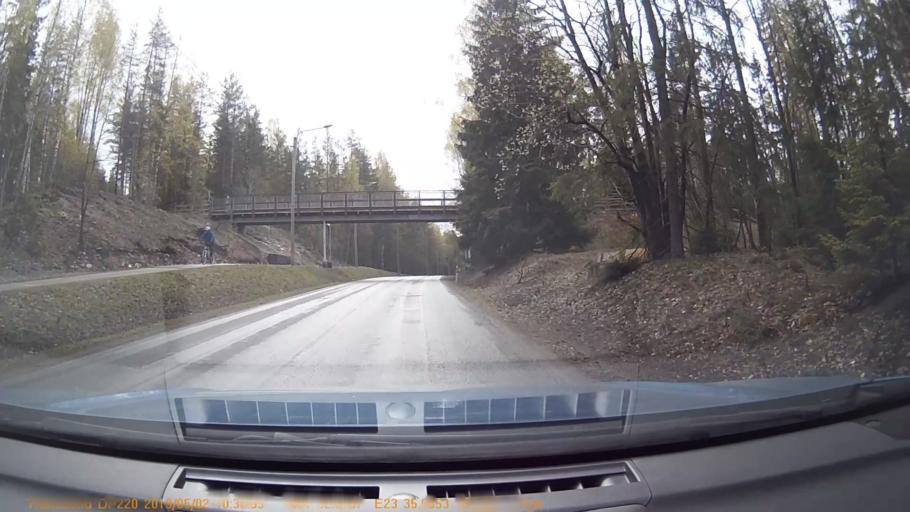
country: FI
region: Pirkanmaa
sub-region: Tampere
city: Yloejaervi
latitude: 61.5436
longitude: 23.5993
